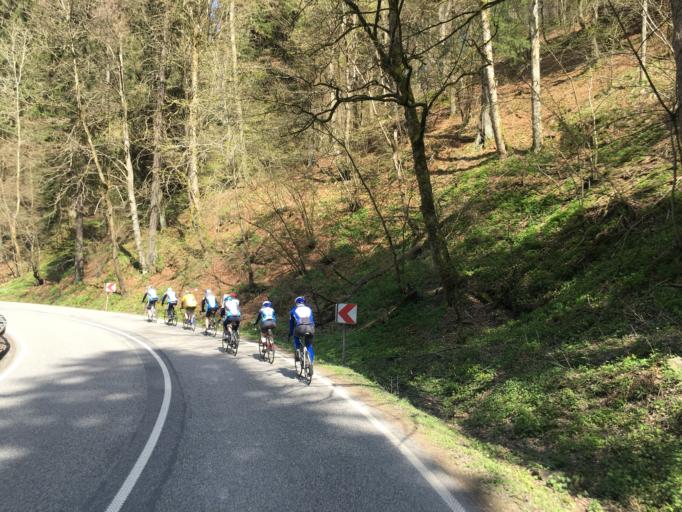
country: DE
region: Thuringia
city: Ilfeld
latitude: 51.6314
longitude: 10.8181
